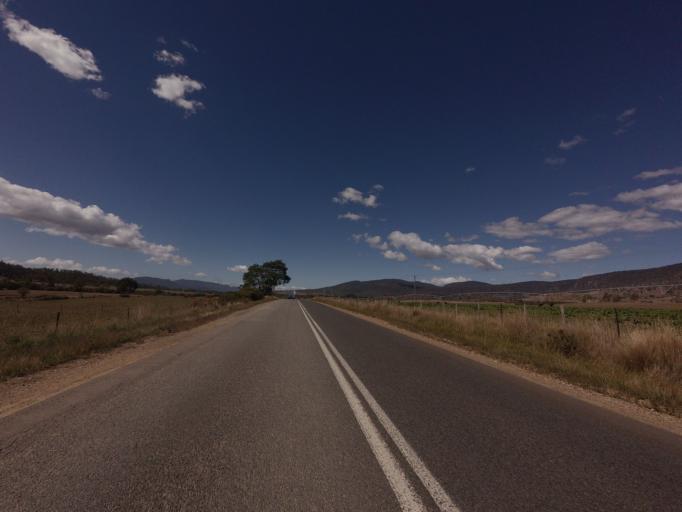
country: AU
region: Tasmania
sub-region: Break O'Day
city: St Helens
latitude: -41.6466
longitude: 147.9393
